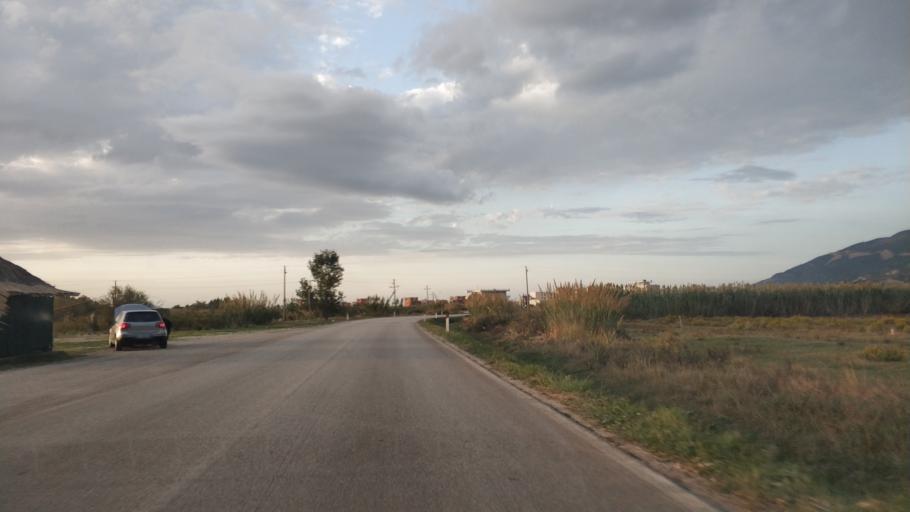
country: AL
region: Vlore
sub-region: Rrethi i Vlores
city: Orikum
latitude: 40.3341
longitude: 19.4772
